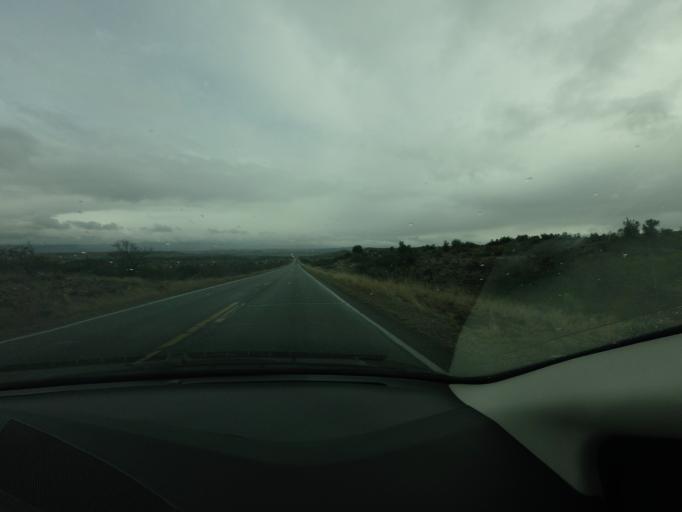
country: US
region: Arizona
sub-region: Yavapai County
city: Cornville
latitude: 34.6836
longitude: -111.8463
